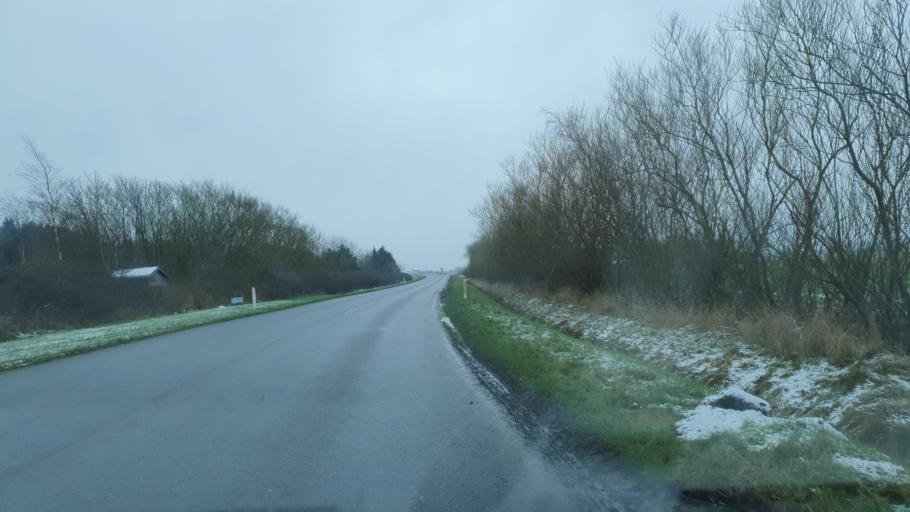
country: DK
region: North Denmark
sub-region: Jammerbugt Kommune
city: Brovst
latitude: 57.0989
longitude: 9.5094
